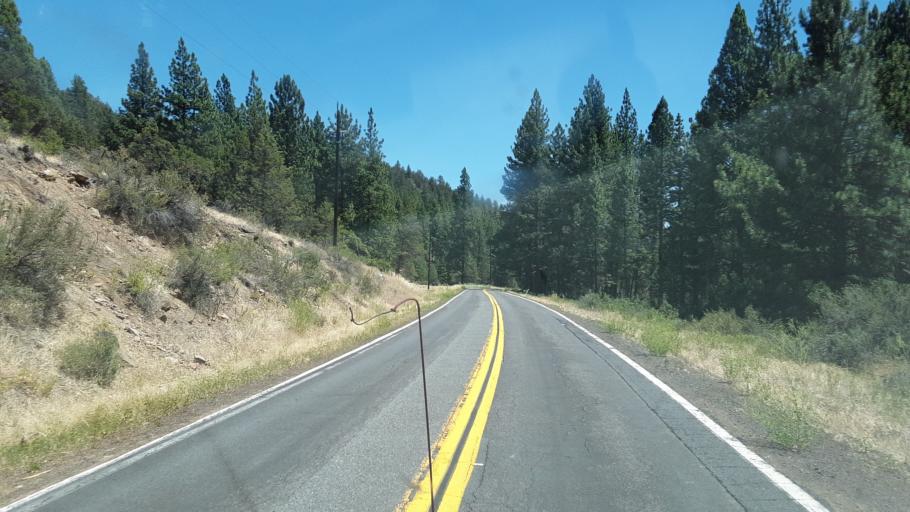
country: US
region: California
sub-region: Modoc County
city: Alturas
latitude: 41.0844
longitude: -120.9025
